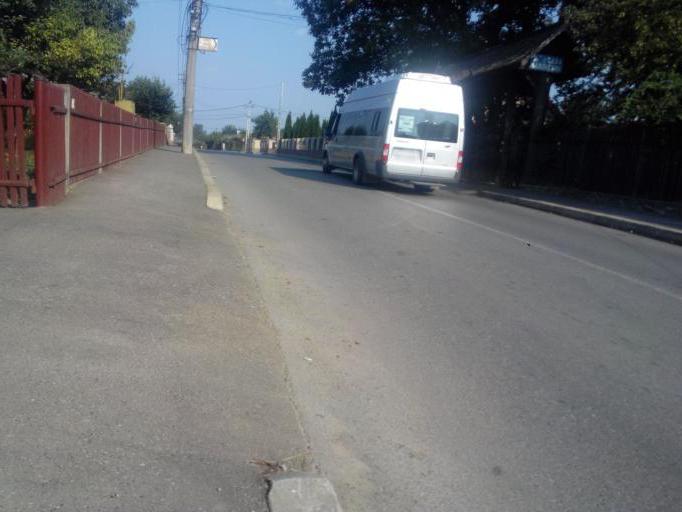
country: RO
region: Suceava
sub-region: Municipiul Falticeni
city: Falticeni
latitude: 47.4657
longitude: 26.2868
